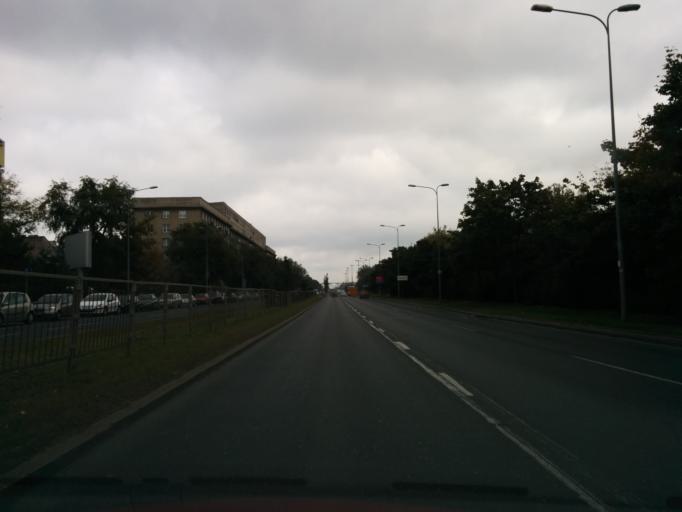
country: PL
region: Masovian Voivodeship
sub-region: Warszawa
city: Praga Polnoc
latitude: 52.2582
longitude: 21.0431
